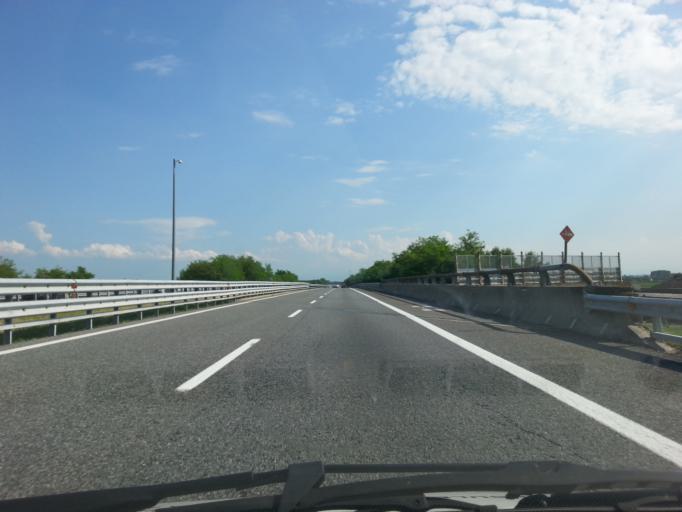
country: IT
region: Piedmont
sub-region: Provincia di Cuneo
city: Caramagna Piemonte
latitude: 44.8087
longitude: 7.7516
